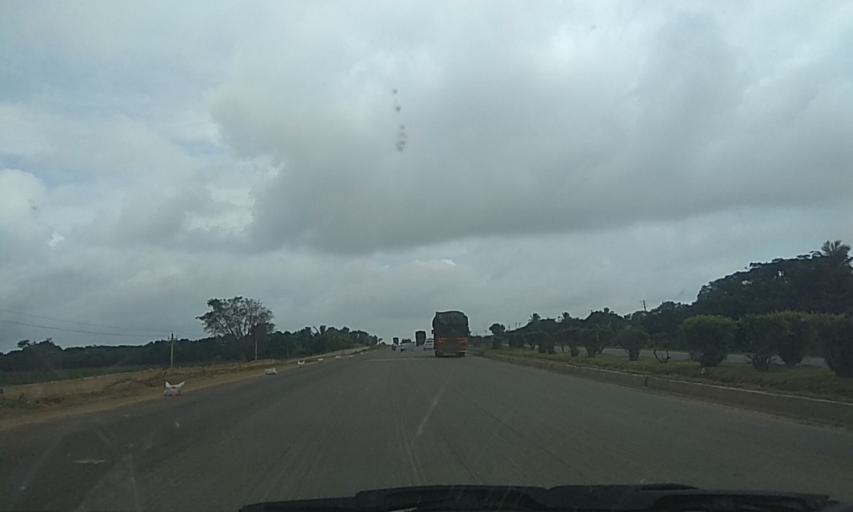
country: IN
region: Karnataka
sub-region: Dharwad
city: Kundgol
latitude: 15.1718
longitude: 75.1401
